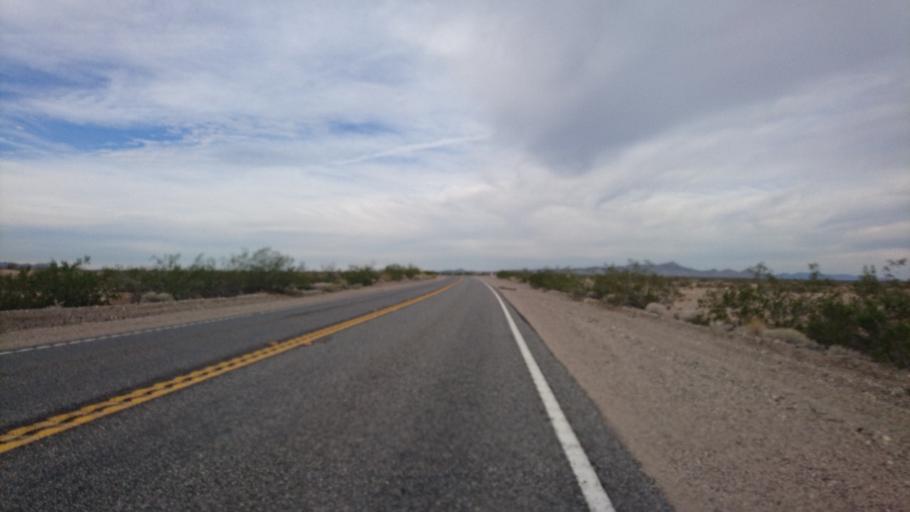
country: US
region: Arizona
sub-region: Mohave County
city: Willow Valley
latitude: 34.9397
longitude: -114.8121
